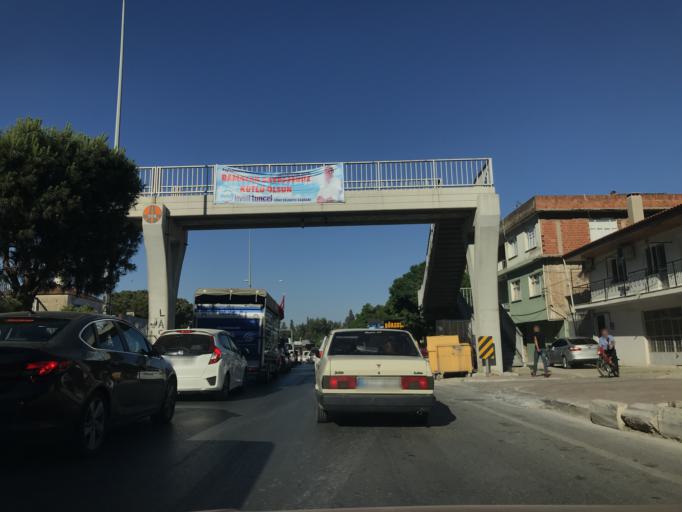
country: TR
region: Aydin
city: Soeke
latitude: 37.7835
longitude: 27.4620
